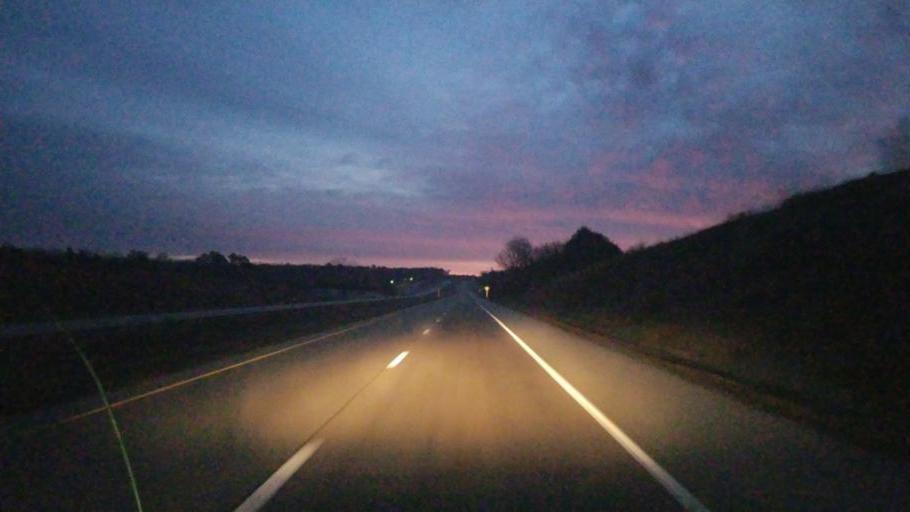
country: US
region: Missouri
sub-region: Shannon County
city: Winona
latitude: 36.9952
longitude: -91.5104
